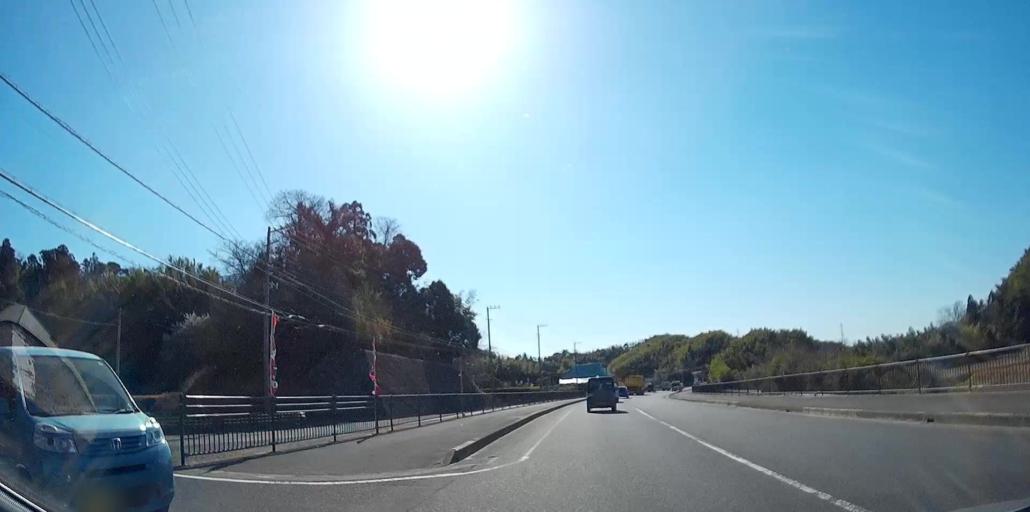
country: JP
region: Chiba
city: Kimitsu
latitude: 35.3009
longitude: 139.9174
